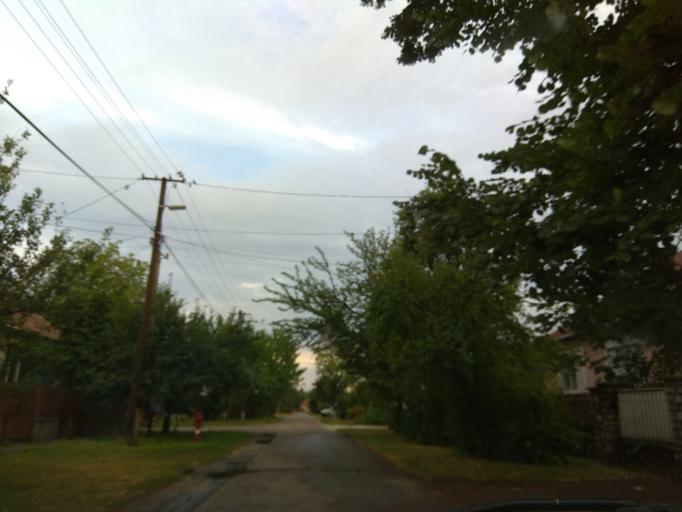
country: HU
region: Borsod-Abauj-Zemplen
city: Miskolc
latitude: 48.0750
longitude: 20.8206
